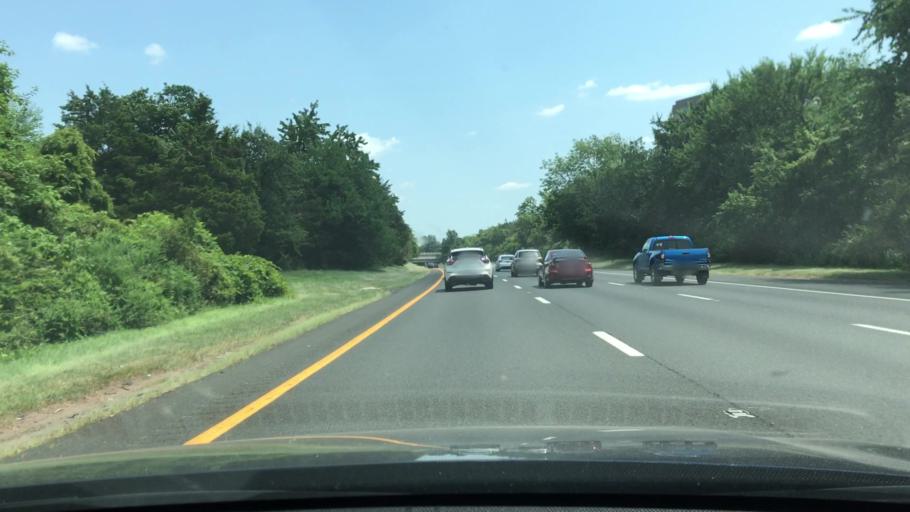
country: US
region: New Jersey
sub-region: Somerset County
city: Somerville
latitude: 40.5853
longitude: -74.6127
